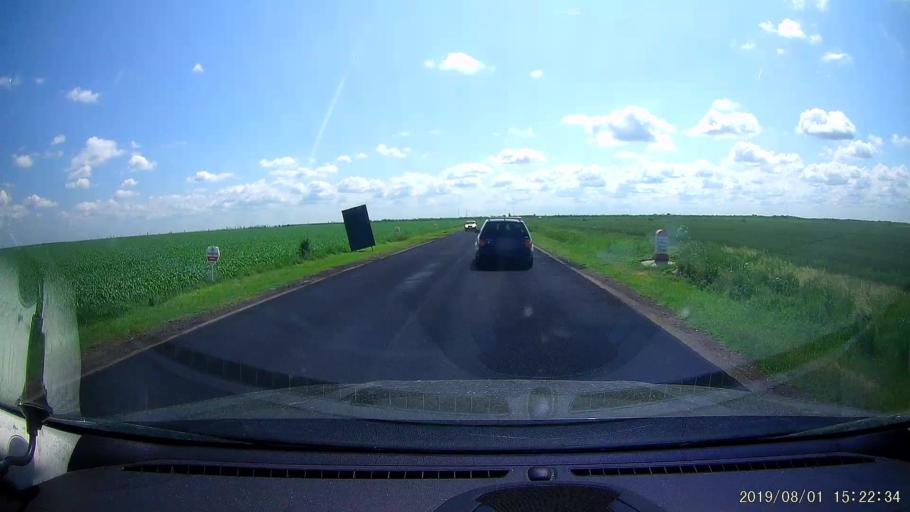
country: RO
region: Braila
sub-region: Comuna Viziru
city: Lanurile
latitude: 45.0518
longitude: 27.7740
